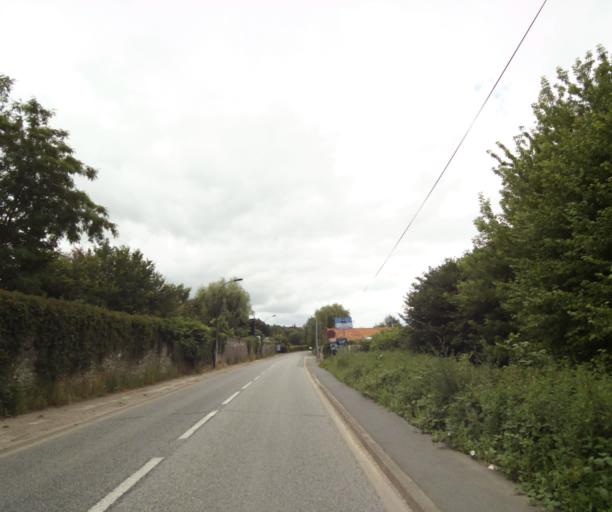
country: FR
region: Ile-de-France
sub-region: Departement des Yvelines
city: Saint-Cyr-l'Ecole
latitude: 48.8104
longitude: 2.0776
